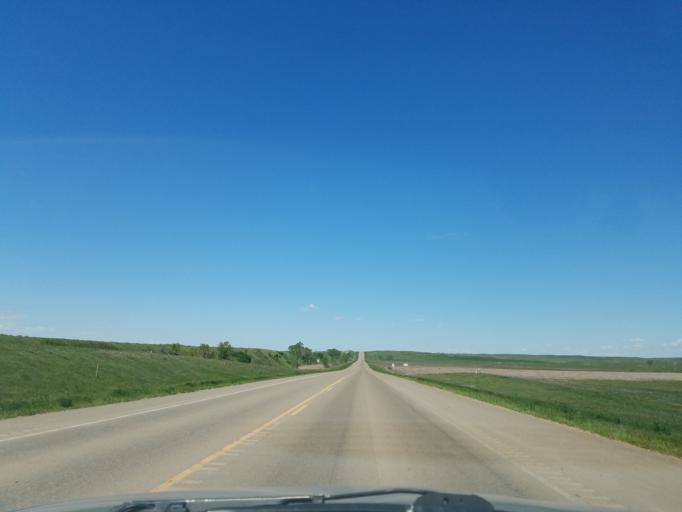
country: US
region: North Dakota
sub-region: McKenzie County
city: Watford City
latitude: 47.7998
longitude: -103.3184
